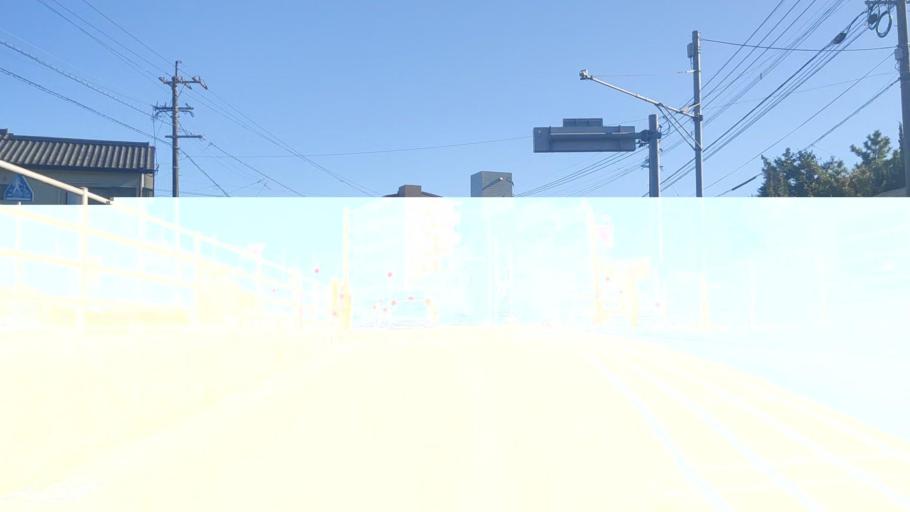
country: JP
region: Miyazaki
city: Miyazaki-shi
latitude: 31.8978
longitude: 131.4267
